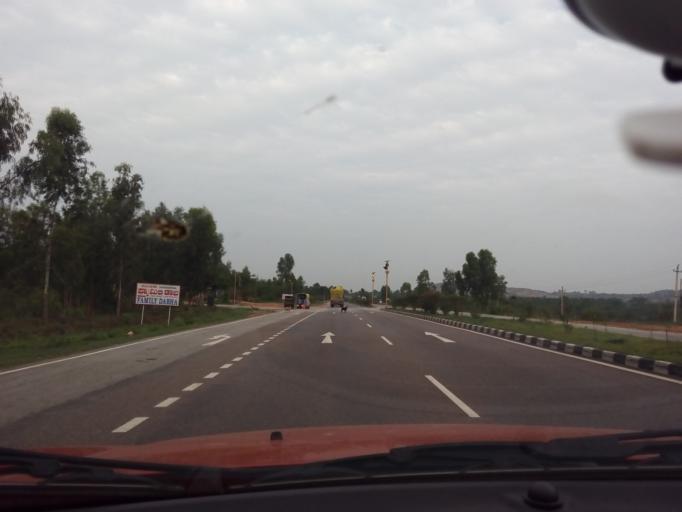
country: IN
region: Karnataka
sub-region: Mandya
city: Belluru
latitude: 12.9717
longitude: 76.8139
